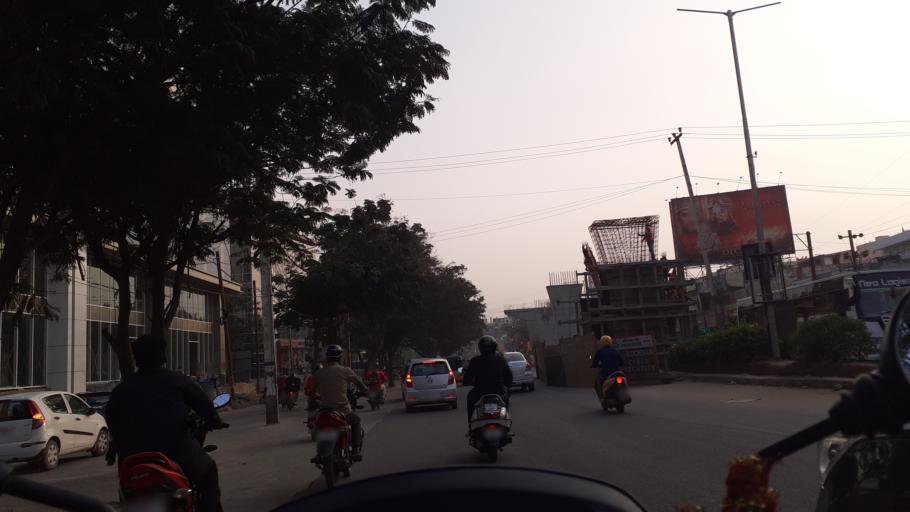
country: IN
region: Telangana
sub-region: Rangareddi
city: Kukatpalli
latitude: 17.4656
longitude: 78.3675
